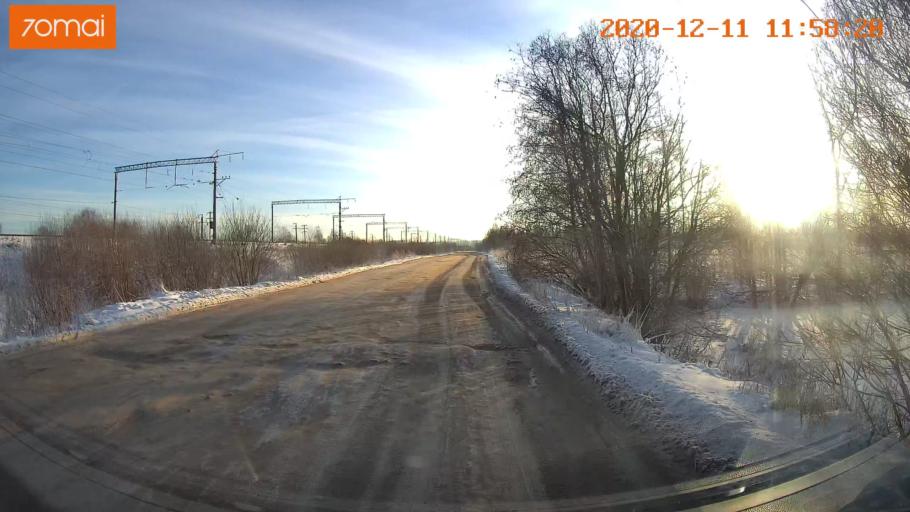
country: RU
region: Kostroma
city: Buy
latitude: 58.4838
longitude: 41.5084
